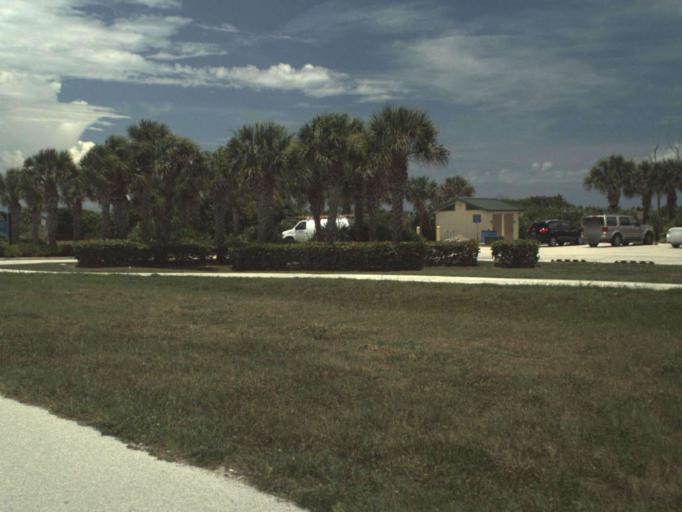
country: US
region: Florida
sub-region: Saint Lucie County
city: Hutchinson Island South
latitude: 27.2967
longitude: -80.2170
